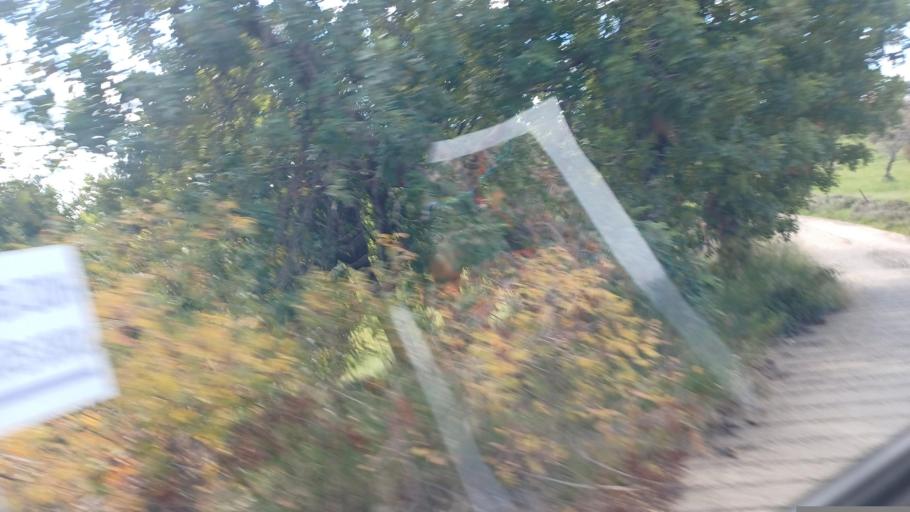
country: CY
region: Limassol
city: Pano Polemidia
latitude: 34.7842
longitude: 32.9763
